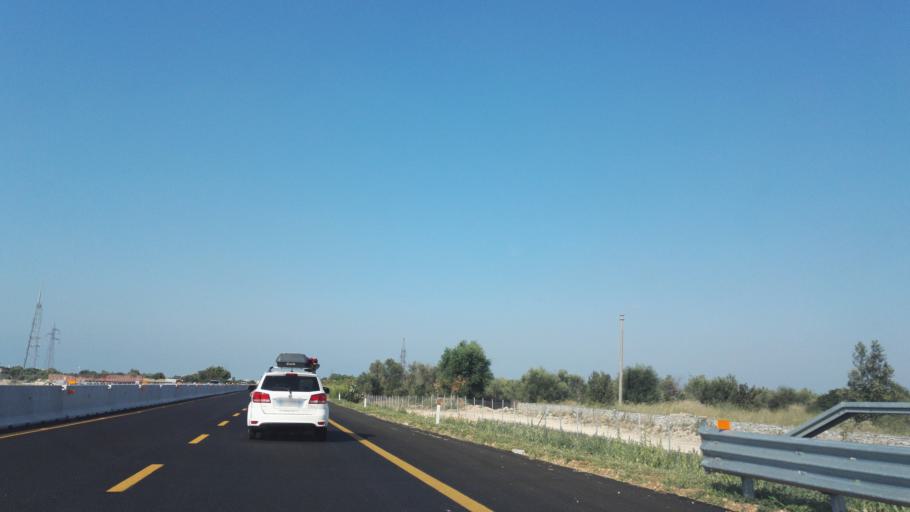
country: IT
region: Apulia
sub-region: Provincia di Bari
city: Modugno
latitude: 41.0902
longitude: 16.8131
